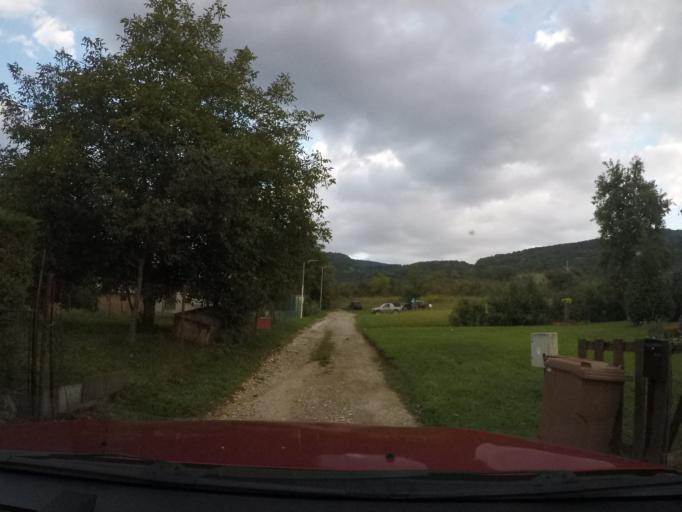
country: SK
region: Kosicky
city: Roznava
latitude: 48.6276
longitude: 20.6202
